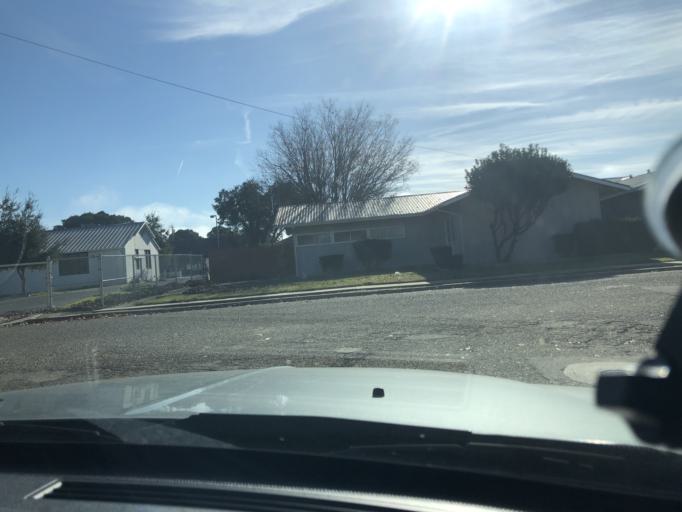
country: US
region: California
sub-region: Monterey County
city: King City
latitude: 36.2065
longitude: -121.1307
